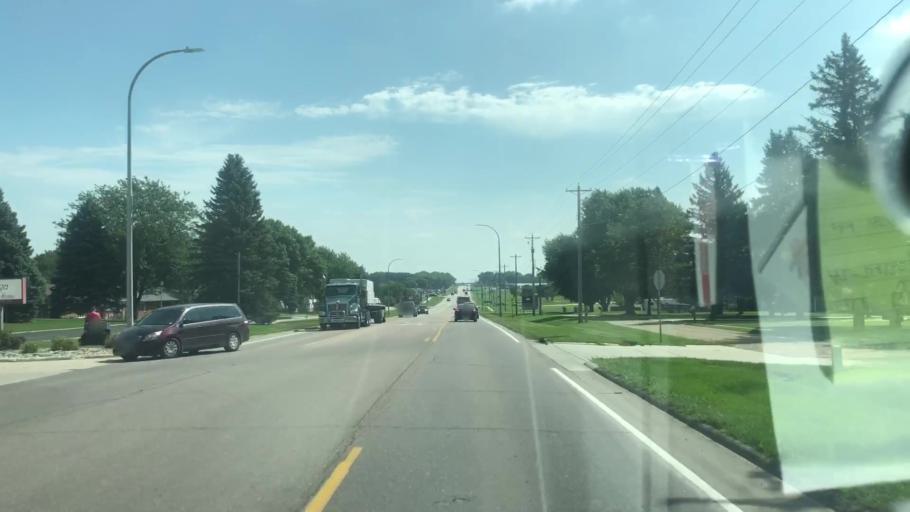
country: US
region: Iowa
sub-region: O'Brien County
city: Sheldon
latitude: 43.1860
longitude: -95.8386
